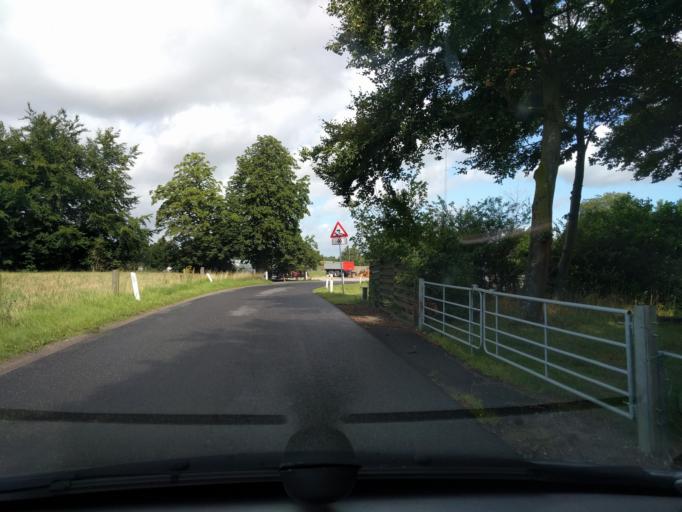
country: DK
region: South Denmark
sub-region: Kerteminde Kommune
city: Langeskov
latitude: 55.3708
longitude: 10.5886
